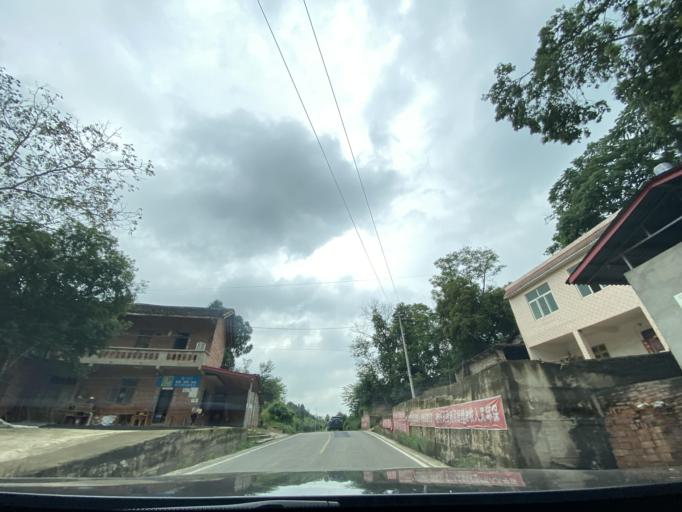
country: CN
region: Sichuan
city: Jiancheng
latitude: 30.5385
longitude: 104.5260
